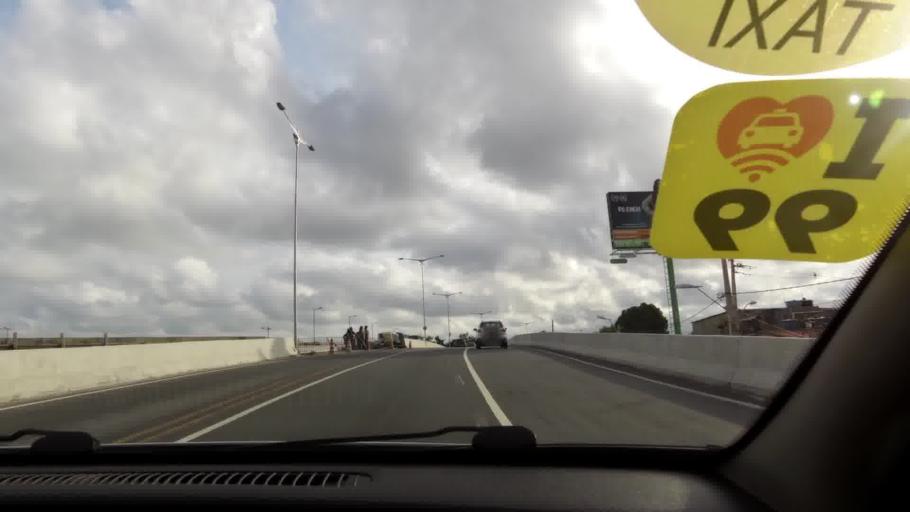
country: BR
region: Pernambuco
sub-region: Recife
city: Recife
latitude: -8.0880
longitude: -34.8916
